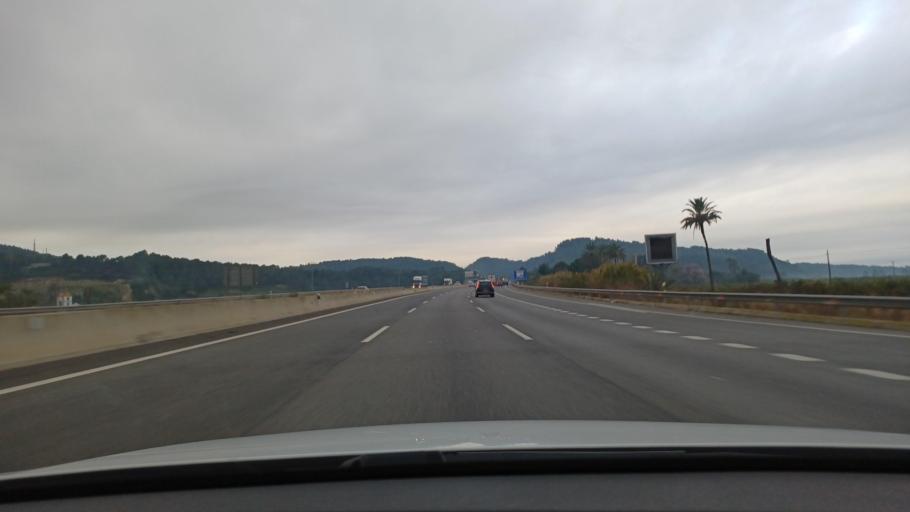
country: ES
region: Valencia
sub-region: Provincia de Valencia
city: Beneixida
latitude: 39.0546
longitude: -0.5453
